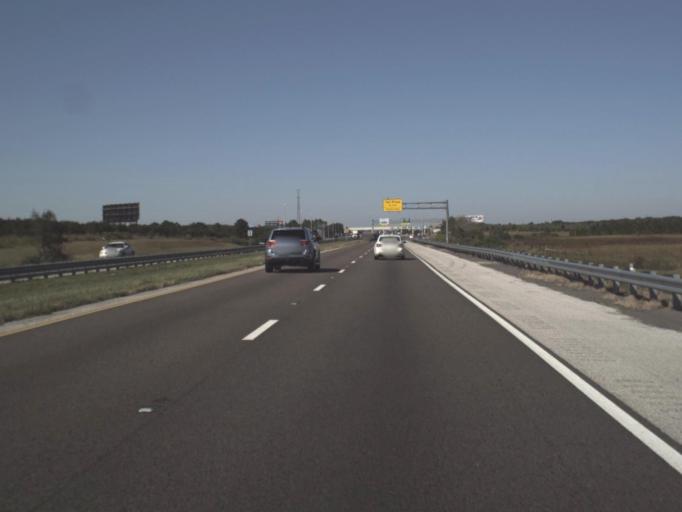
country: US
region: Florida
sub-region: Lake County
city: Yalaha
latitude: 28.6651
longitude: -81.8329
